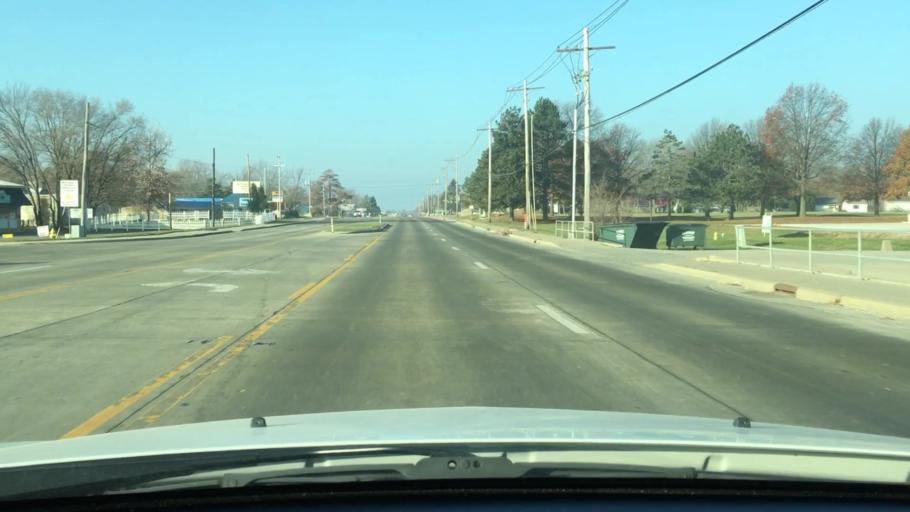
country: US
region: Illinois
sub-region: Woodford County
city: Germantown Hills
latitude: 40.6929
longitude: -89.4846
